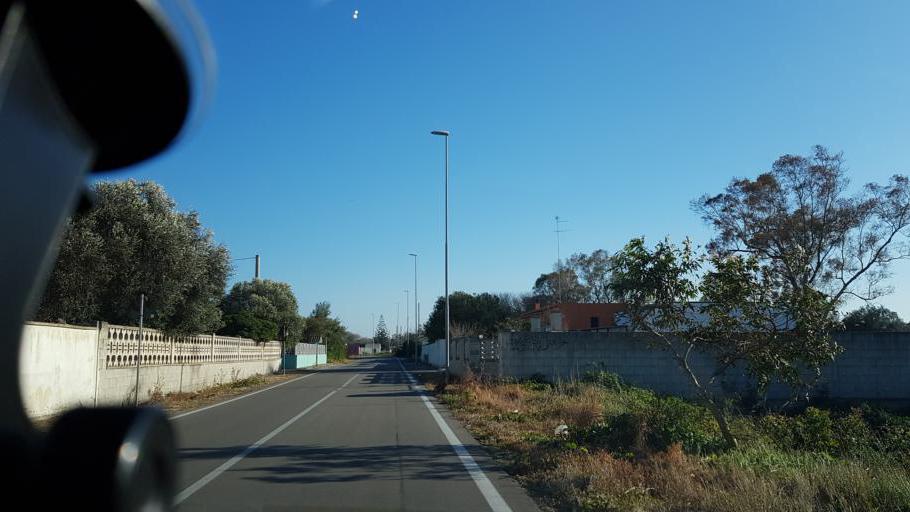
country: IT
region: Apulia
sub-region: Provincia di Lecce
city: Merine
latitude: 40.4298
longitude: 18.2424
